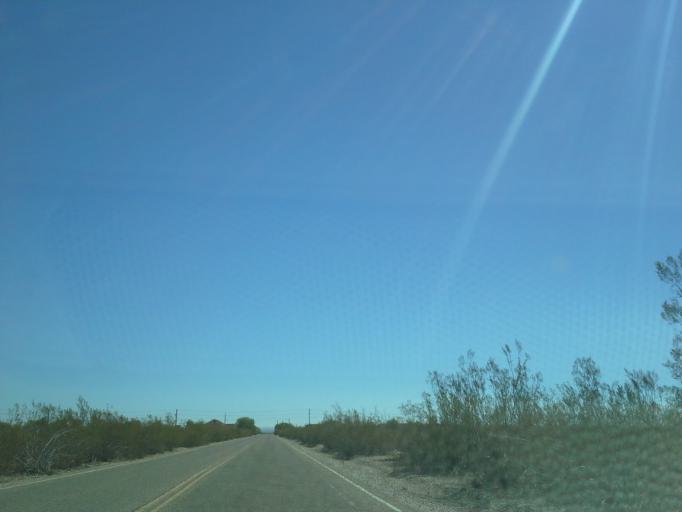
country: US
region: Arizona
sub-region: Pinal County
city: Coolidge
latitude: 32.9954
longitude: -111.5279
